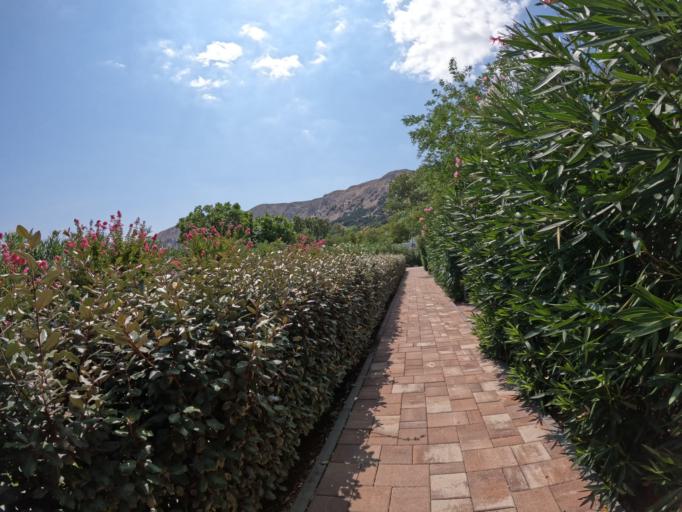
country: HR
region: Primorsko-Goranska
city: Punat
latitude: 44.9657
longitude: 14.7448
